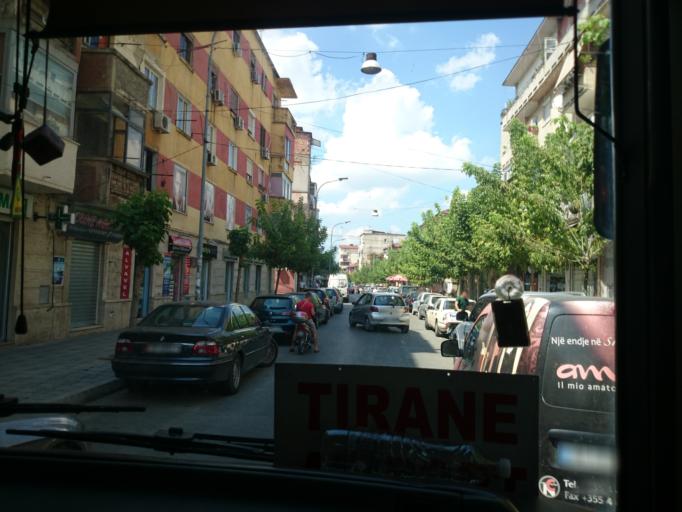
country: AL
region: Tirane
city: Tirana
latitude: 41.3302
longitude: 19.8141
